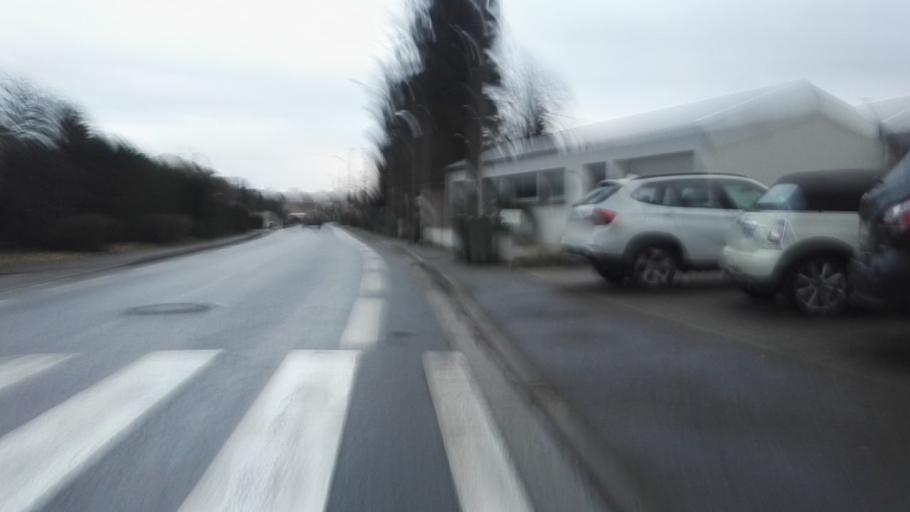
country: FR
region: Aquitaine
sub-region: Departement de la Gironde
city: Merignac
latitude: 44.8327
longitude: -0.6361
